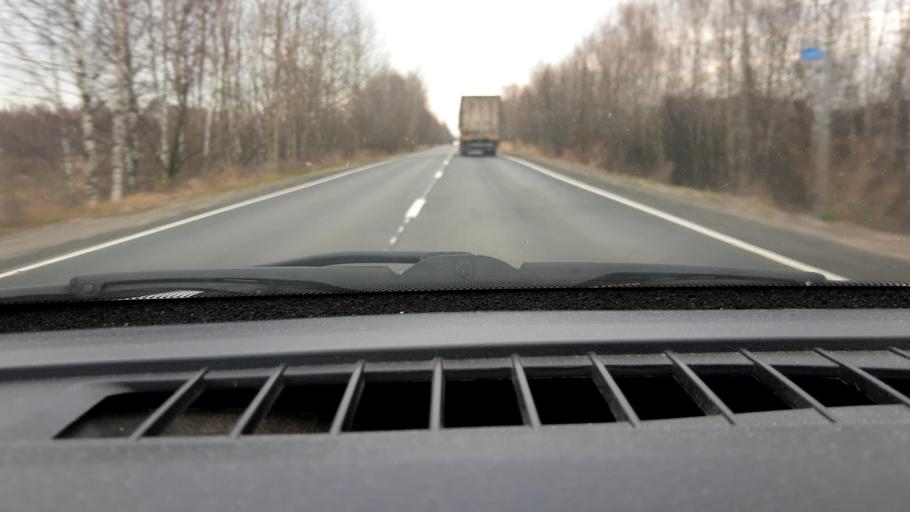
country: RU
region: Nizjnij Novgorod
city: Lukino
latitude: 56.5358
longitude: 43.7866
